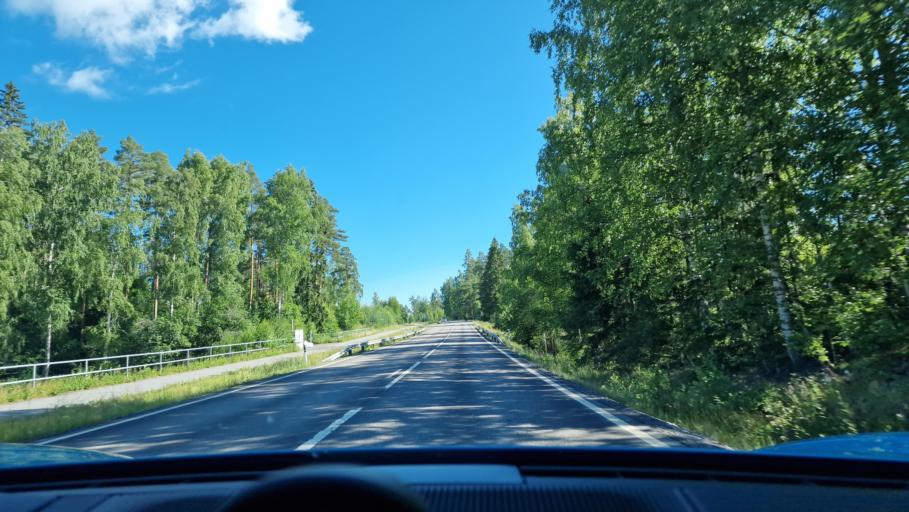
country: FI
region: Pirkanmaa
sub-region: Tampere
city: Kangasala
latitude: 61.4820
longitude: 24.1504
